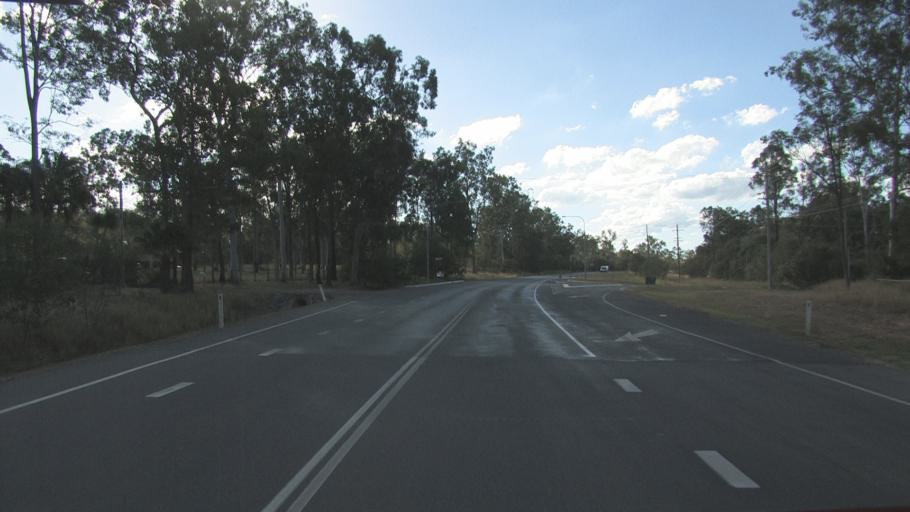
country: AU
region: Queensland
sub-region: Logan
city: North Maclean
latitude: -27.7767
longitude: 152.9806
